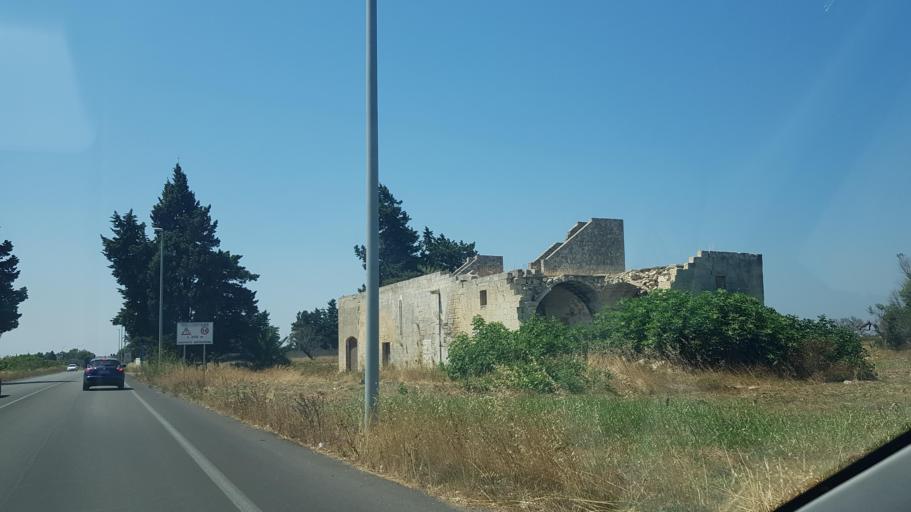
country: IT
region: Apulia
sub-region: Provincia di Lecce
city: Merine
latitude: 40.3386
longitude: 18.2269
